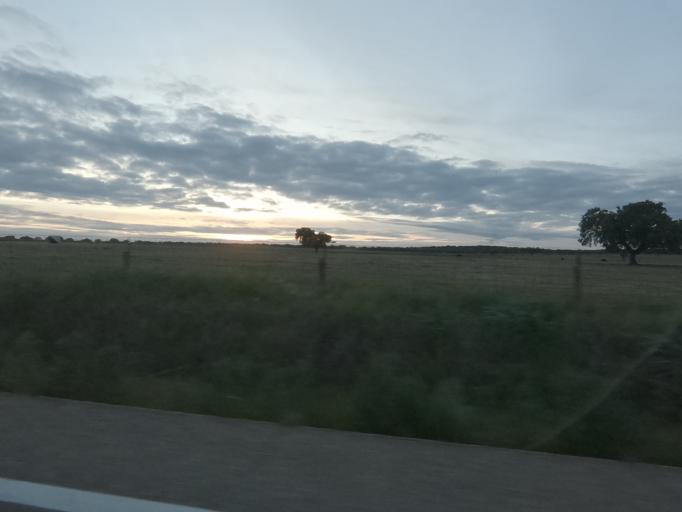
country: ES
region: Extremadura
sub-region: Provincia de Badajoz
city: Badajoz
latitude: 38.9702
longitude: -6.8938
